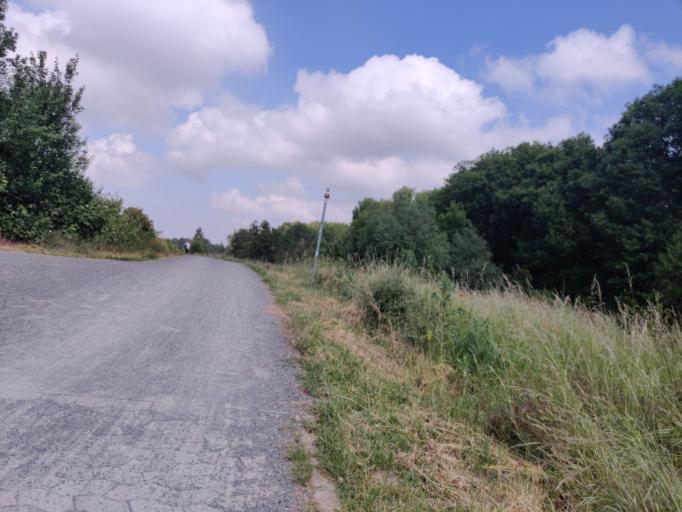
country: DE
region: Lower Saxony
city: Hildesheim
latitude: 52.1313
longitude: 9.9587
